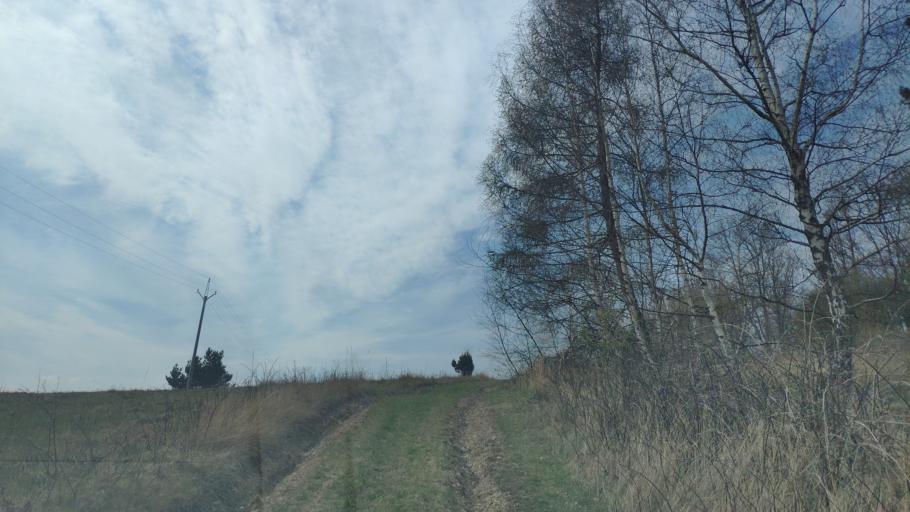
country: SK
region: Kosicky
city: Moldava nad Bodvou
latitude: 48.7488
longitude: 21.0215
